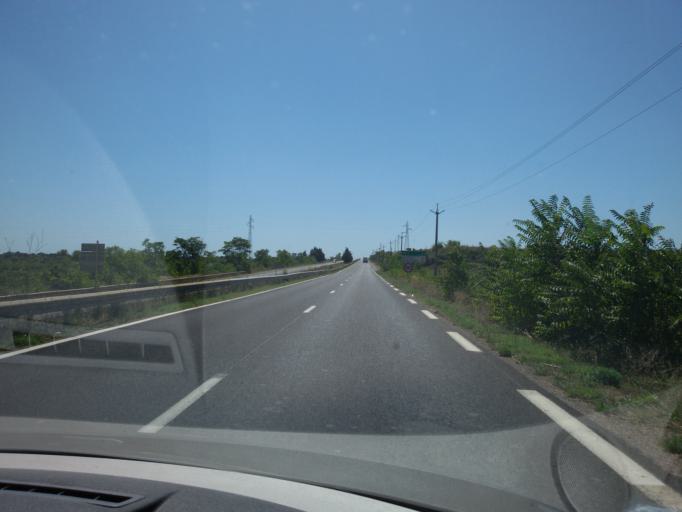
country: FR
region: Languedoc-Roussillon
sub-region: Departement de l'Herault
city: Saint-Jean-de-Vedas
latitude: 43.5425
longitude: 3.8229
